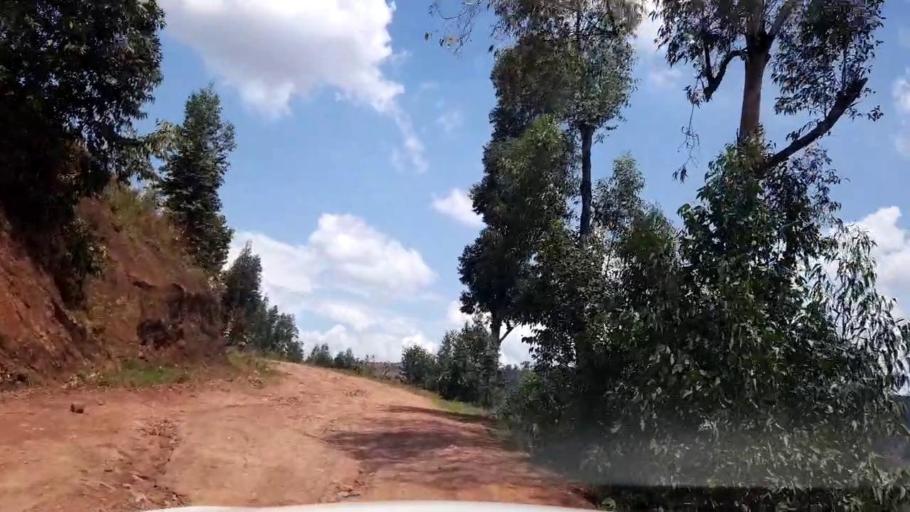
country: RW
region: Northern Province
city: Byumba
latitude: -1.5260
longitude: 30.1753
